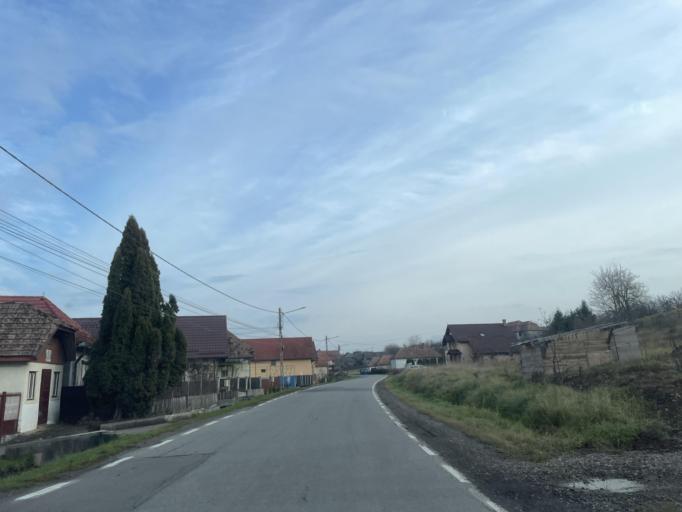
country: RO
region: Mures
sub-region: Comuna Solovastru
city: Solovastru
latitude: 46.7762
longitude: 24.7523
